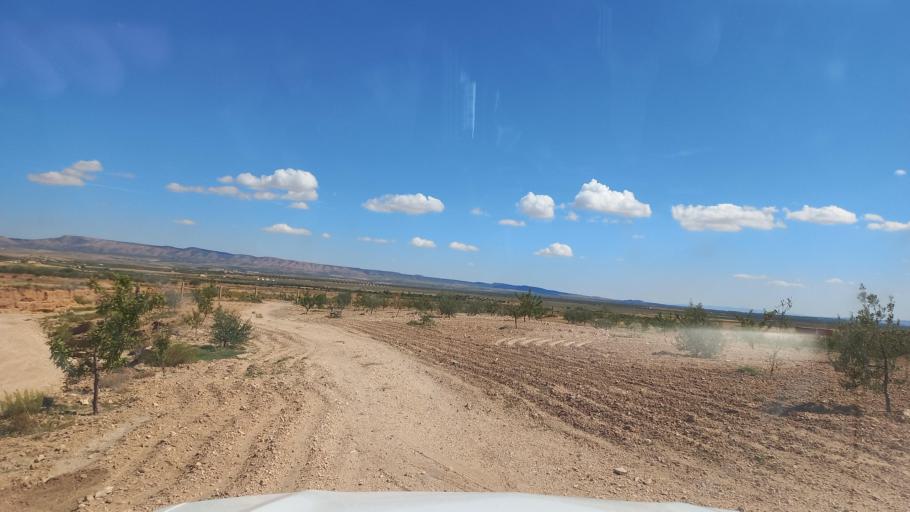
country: TN
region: Al Qasrayn
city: Sbiba
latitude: 35.3531
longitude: 9.0187
